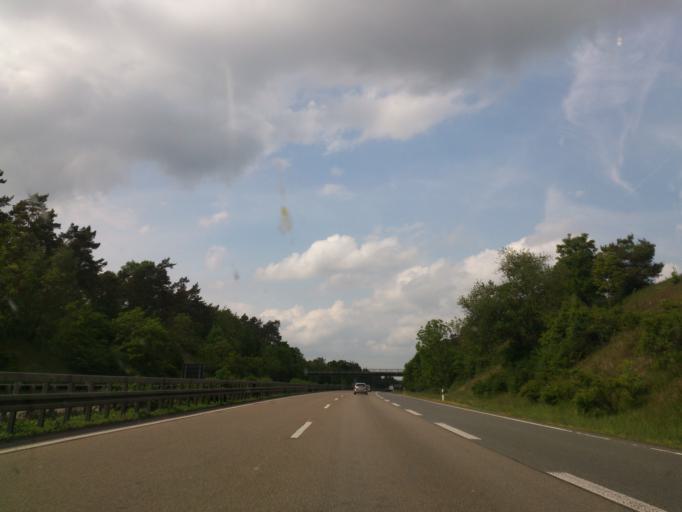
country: DE
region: Hesse
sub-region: Regierungsbezirk Kassel
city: Breuna
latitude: 51.4182
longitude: 9.1595
